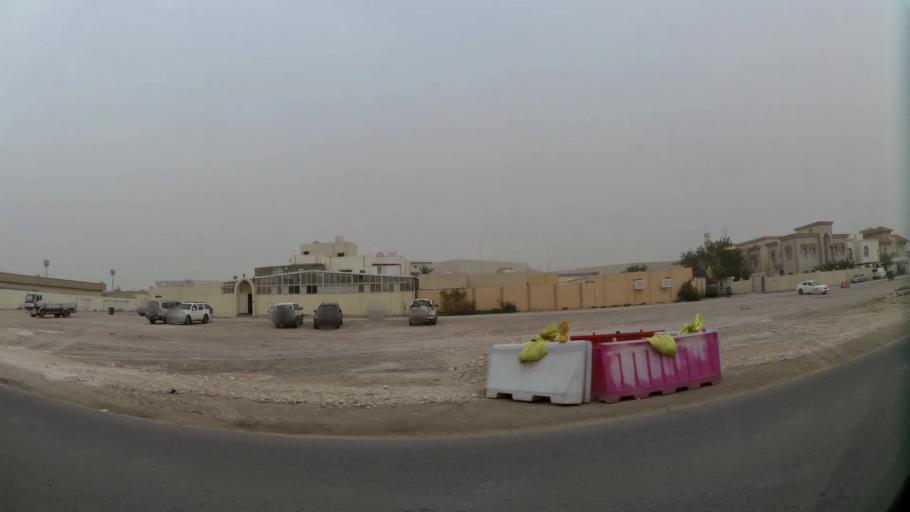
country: QA
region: Baladiyat ad Dawhah
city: Doha
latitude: 25.2352
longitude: 51.5035
